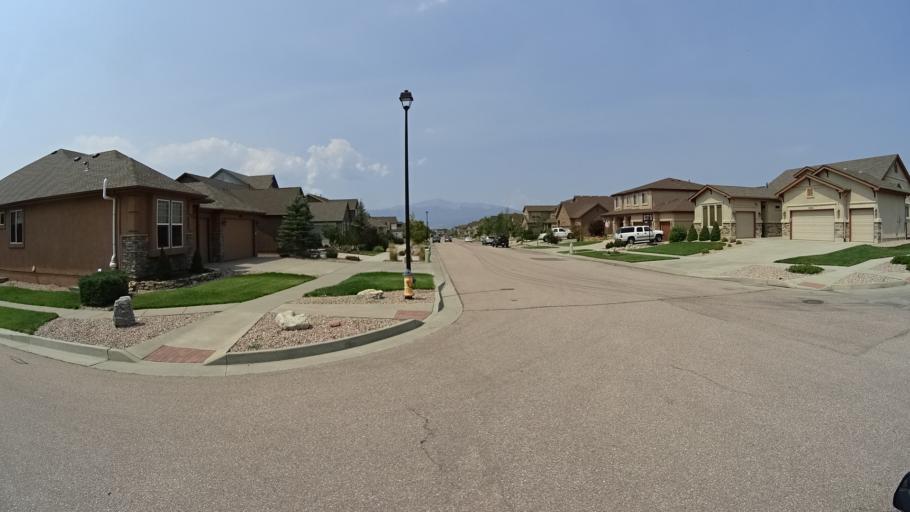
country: US
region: Colorado
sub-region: El Paso County
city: Black Forest
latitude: 38.9683
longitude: -104.7206
